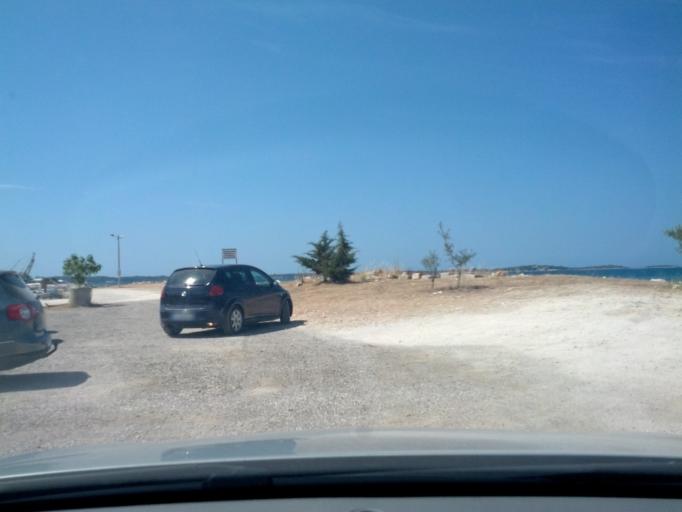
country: HR
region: Istarska
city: Fazana
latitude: 44.9565
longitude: 13.7848
